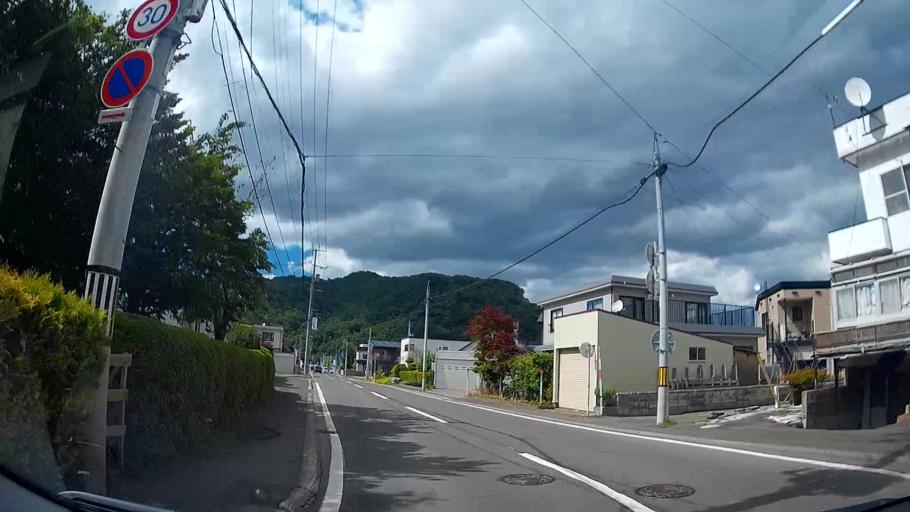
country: JP
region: Hokkaido
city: Sapporo
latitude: 42.9592
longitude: 141.3202
